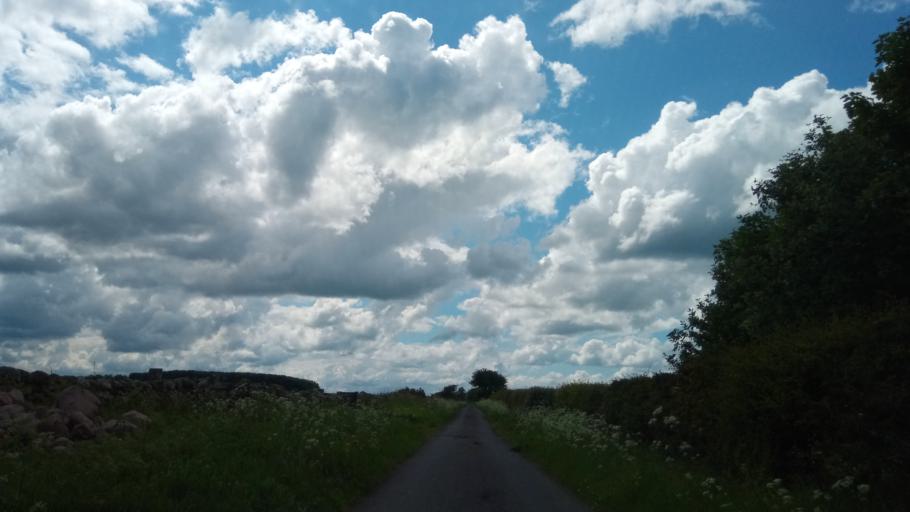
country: GB
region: Scotland
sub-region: The Scottish Borders
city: Coldstream
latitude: 55.5988
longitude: -2.2765
